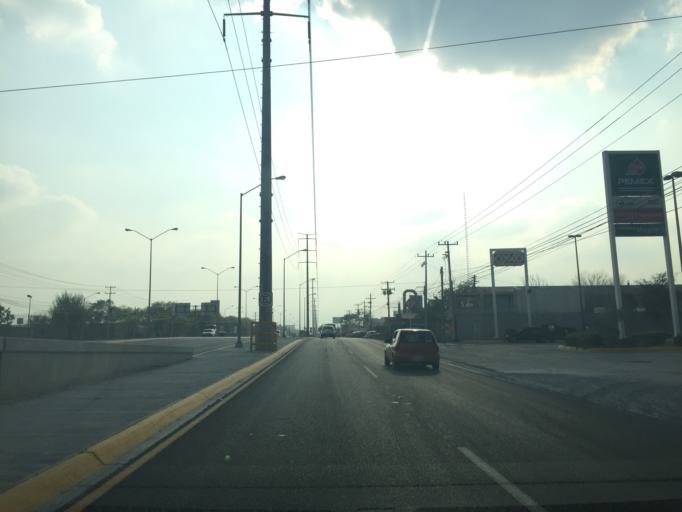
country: MX
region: Nuevo Leon
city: Apodaca
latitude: 25.7667
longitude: -100.2005
